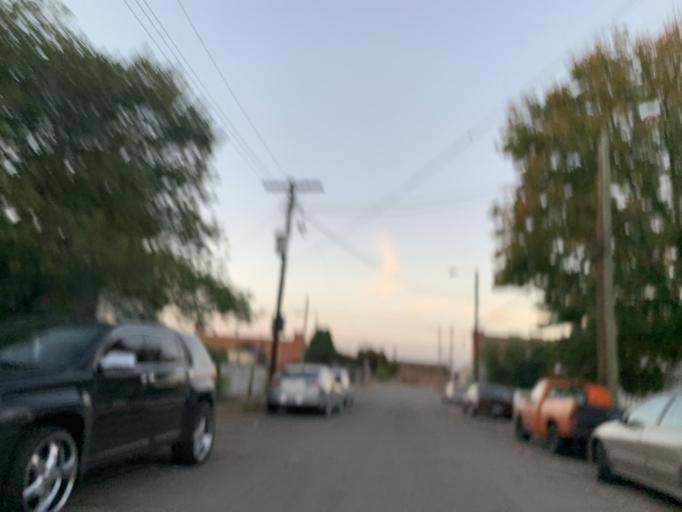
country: US
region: Kentucky
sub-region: Jefferson County
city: Louisville
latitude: 38.2288
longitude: -85.7699
